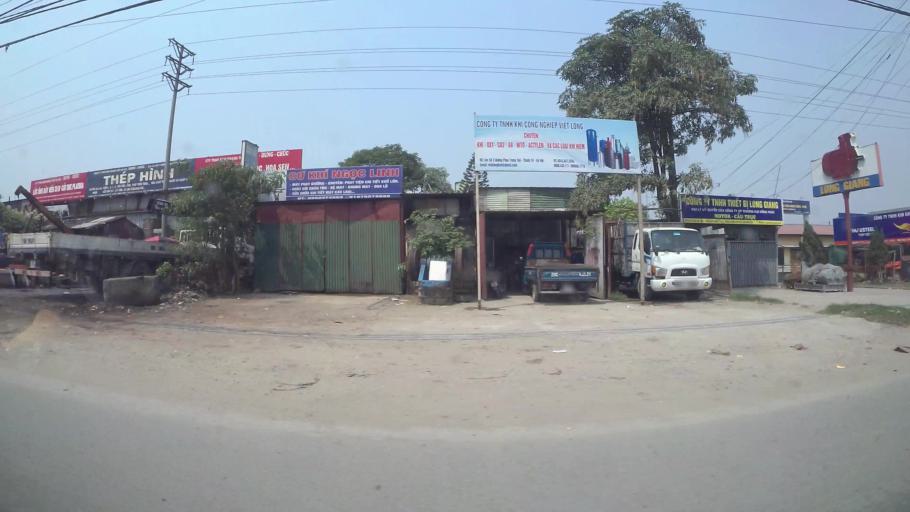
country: VN
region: Ha Noi
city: Van Dien
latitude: 20.9475
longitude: 105.8261
